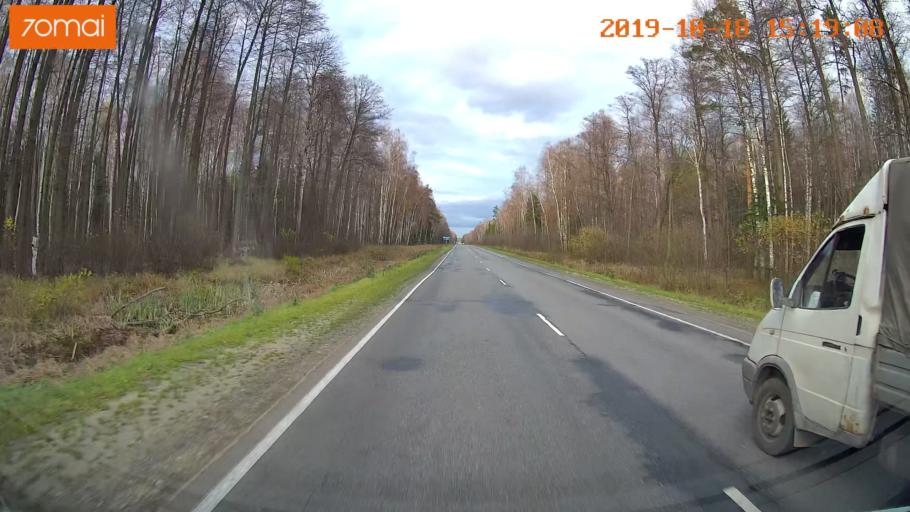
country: RU
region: Vladimir
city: Anopino
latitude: 55.6685
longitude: 40.7353
